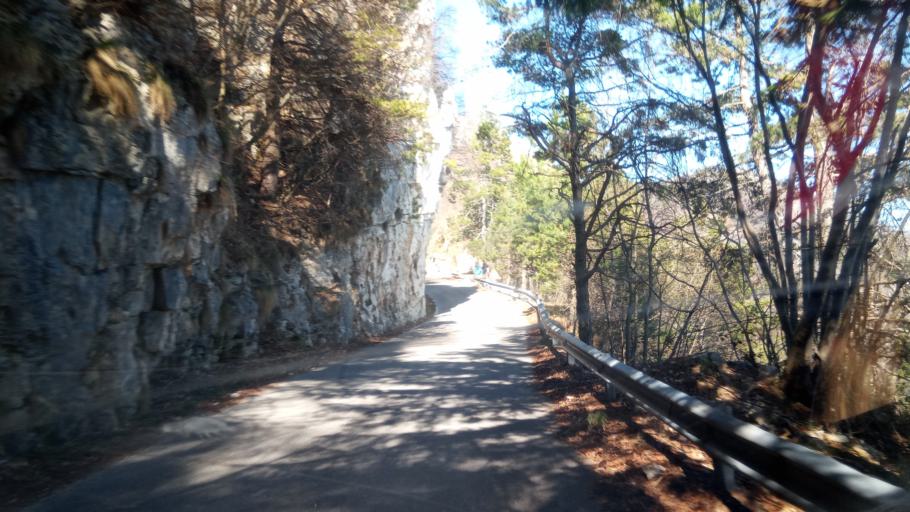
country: IT
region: Veneto
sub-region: Provincia di Treviso
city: Borso del Grappa
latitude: 45.8297
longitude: 11.7711
